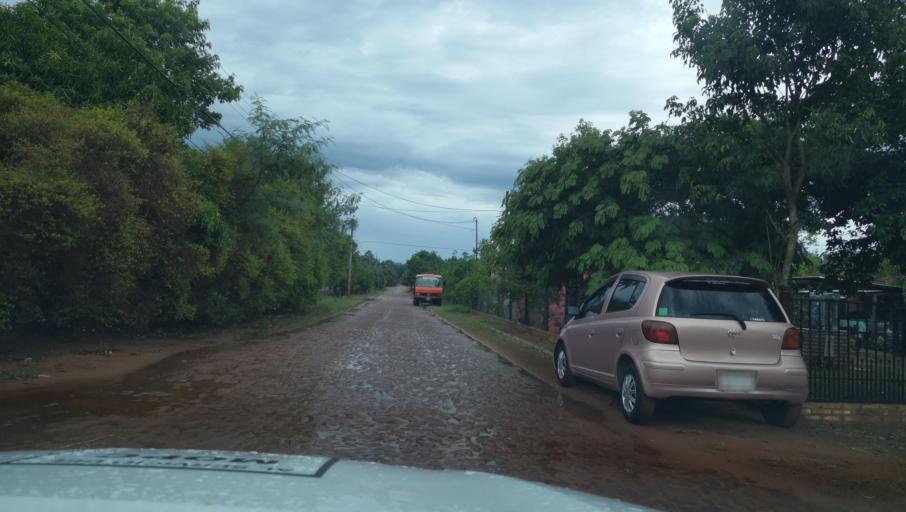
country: PY
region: Misiones
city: Santa Maria
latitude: -26.8978
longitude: -57.0347
